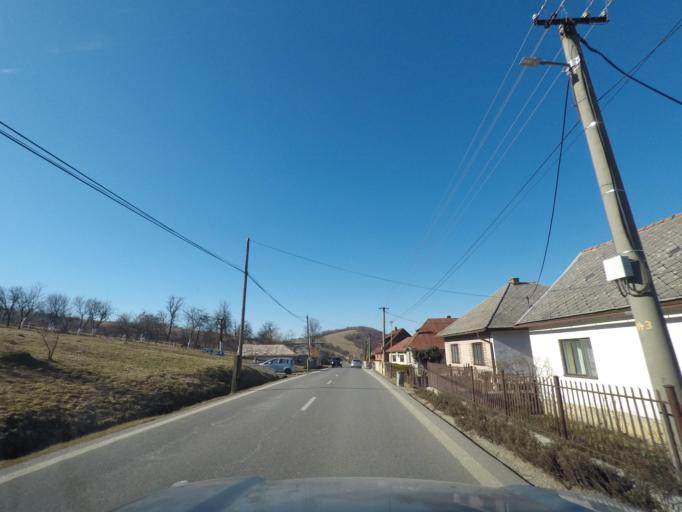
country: SK
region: Presovsky
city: Snina
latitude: 48.9609
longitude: 22.2531
